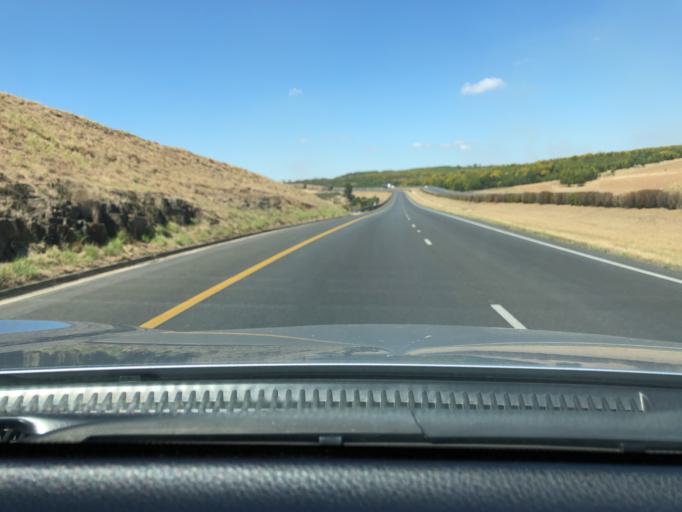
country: ZA
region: KwaZulu-Natal
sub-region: uMgungundlovu District Municipality
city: Mooirivier
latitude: -29.1170
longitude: 29.9481
